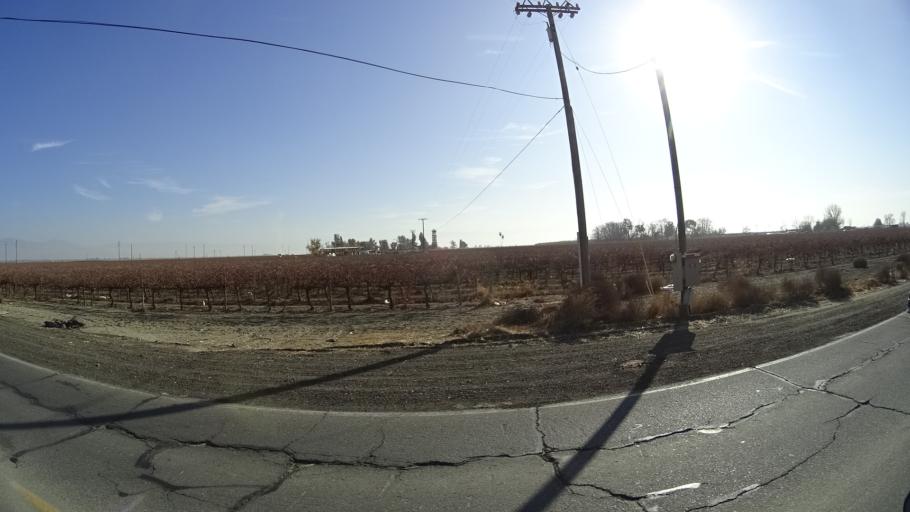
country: US
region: California
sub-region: Kern County
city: Greenfield
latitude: 35.2962
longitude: -118.9789
